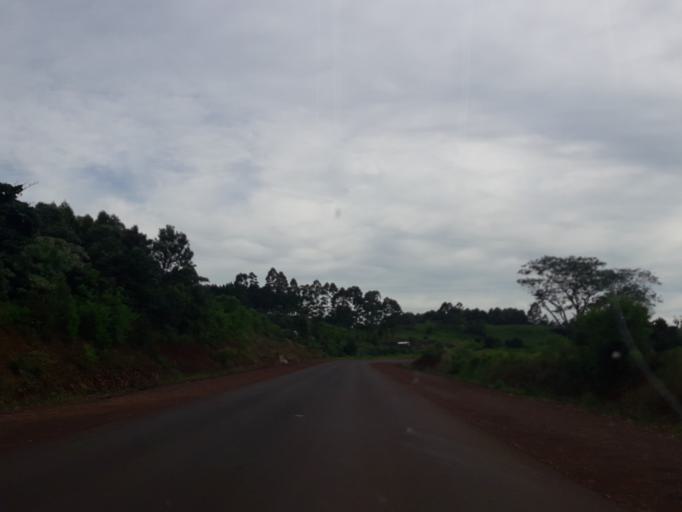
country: AR
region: Misiones
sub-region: Departamento de San Pedro
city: San Pedro
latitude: -26.5158
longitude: -53.9347
